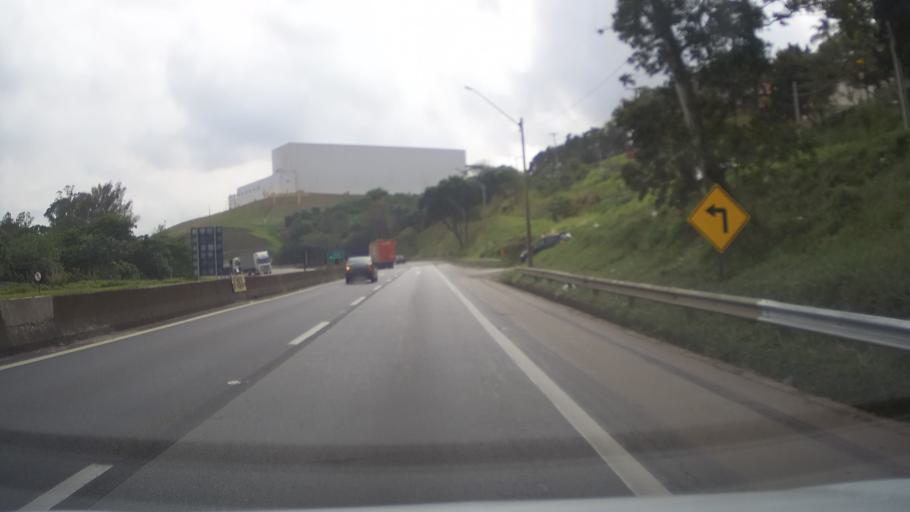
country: BR
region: Minas Gerais
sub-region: Extrema
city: Extrema
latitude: -22.8176
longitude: -46.2945
